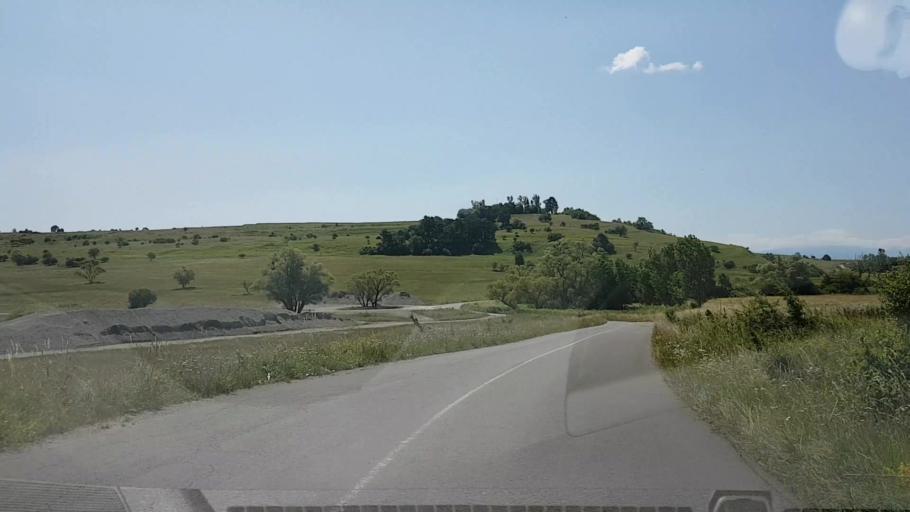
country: RO
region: Brasov
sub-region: Comuna Cincu
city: Cincu
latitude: 45.9538
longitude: 24.7826
